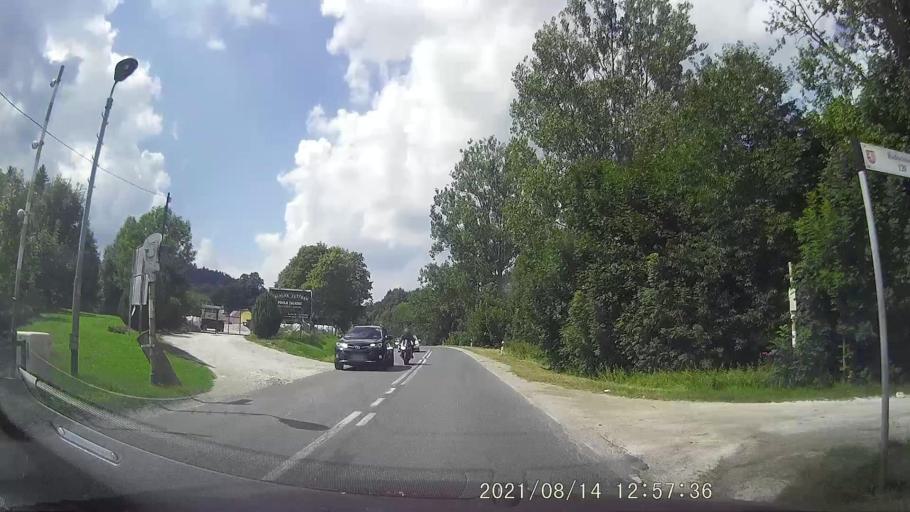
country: PL
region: Lower Silesian Voivodeship
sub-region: Powiat klodzki
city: Ladek-Zdroj
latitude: 50.3397
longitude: 16.8255
